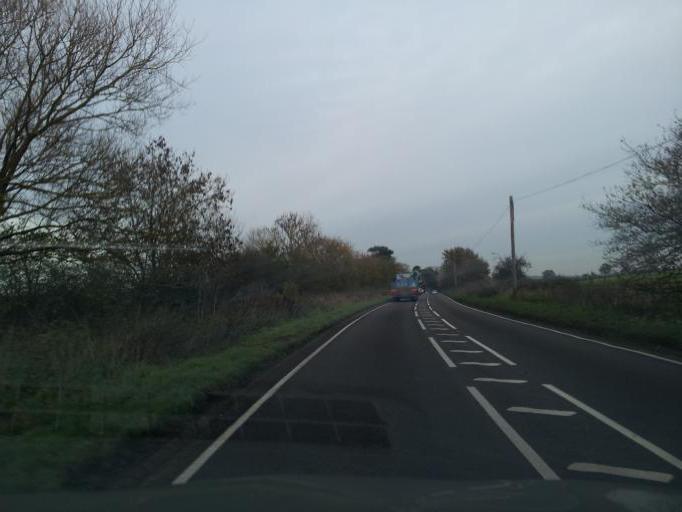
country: GB
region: England
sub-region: Buckinghamshire
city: Stewkley
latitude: 51.8740
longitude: -0.7521
